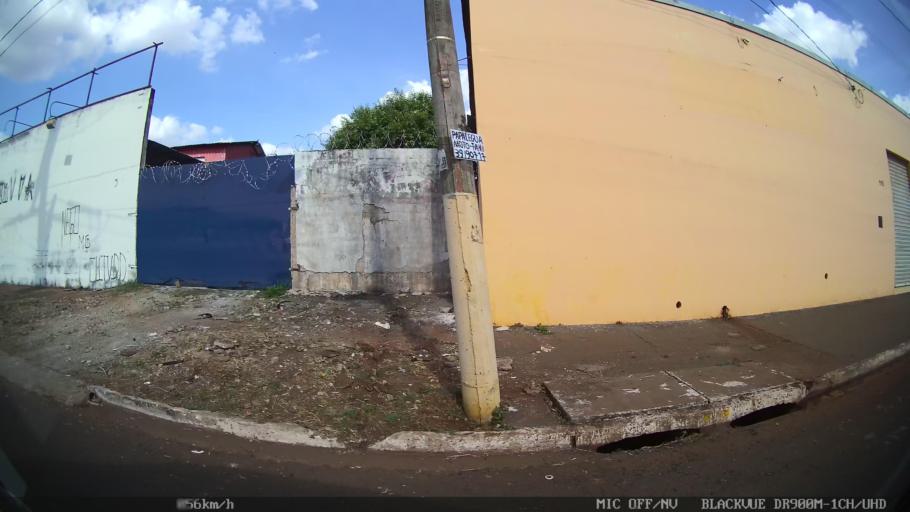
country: BR
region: Sao Paulo
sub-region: Ribeirao Preto
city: Ribeirao Preto
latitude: -21.1790
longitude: -47.8236
